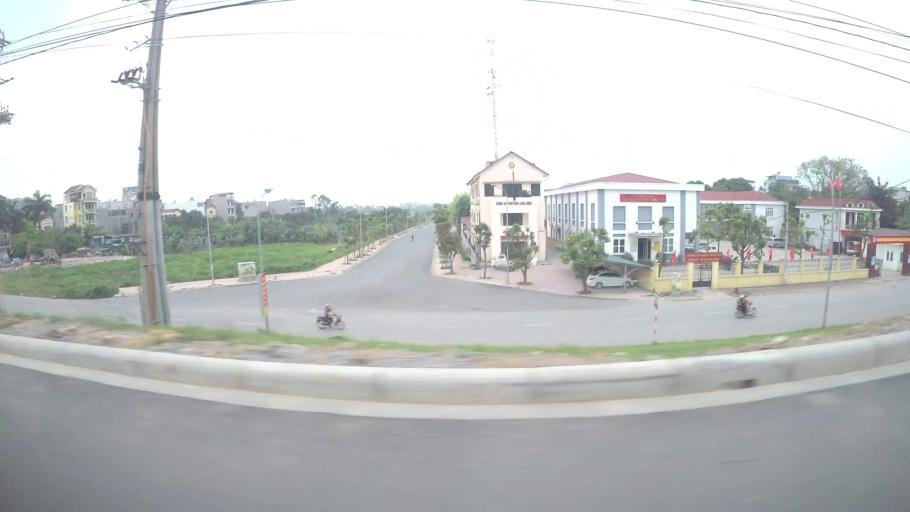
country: VN
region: Ha Noi
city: Hoan Kiem
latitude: 21.0227
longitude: 105.8885
